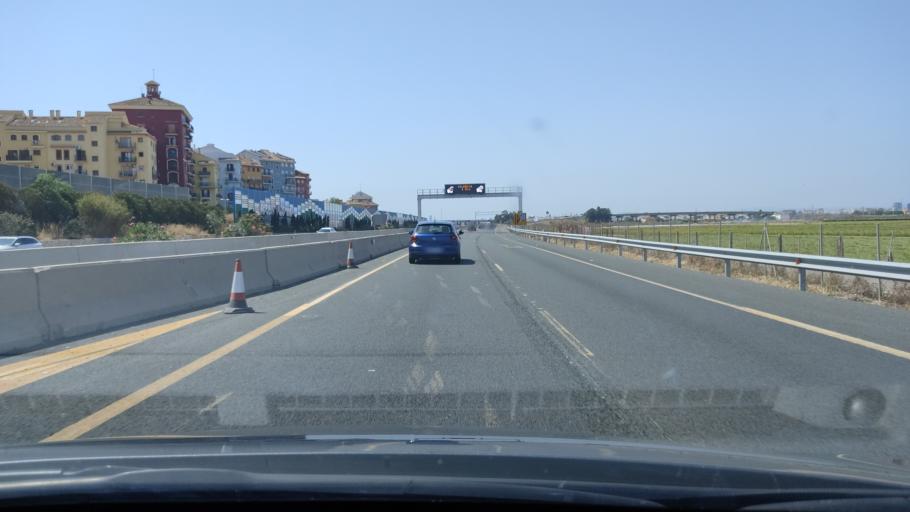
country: ES
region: Valencia
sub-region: Provincia de Valencia
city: Meliana
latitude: 39.5147
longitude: -0.3214
